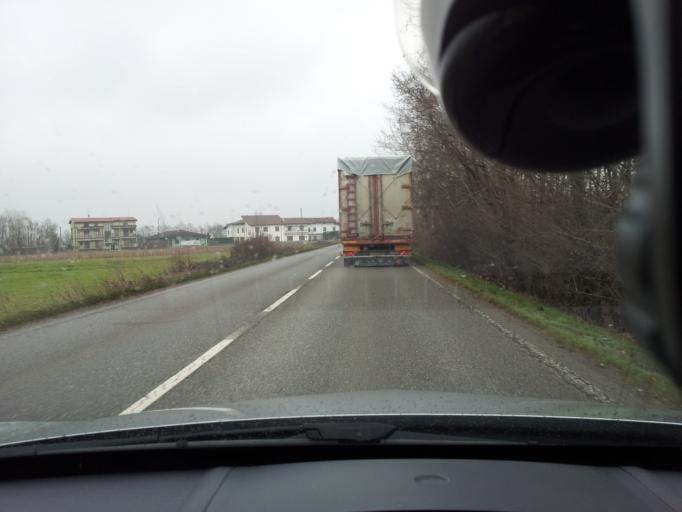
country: IT
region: Lombardy
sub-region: Provincia di Bergamo
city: Calcinate
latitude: 45.6109
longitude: 9.7909
